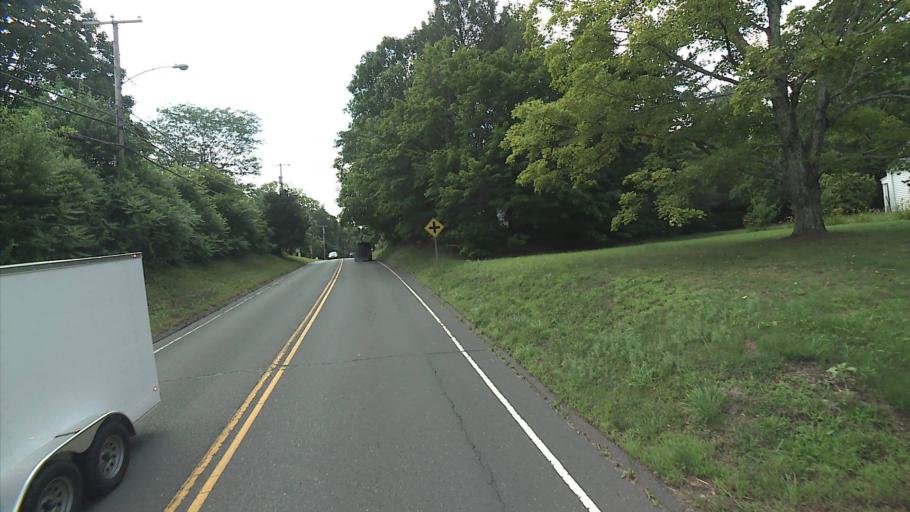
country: US
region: Connecticut
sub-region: Hartford County
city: Glastonbury Center
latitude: 41.6579
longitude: -72.6046
